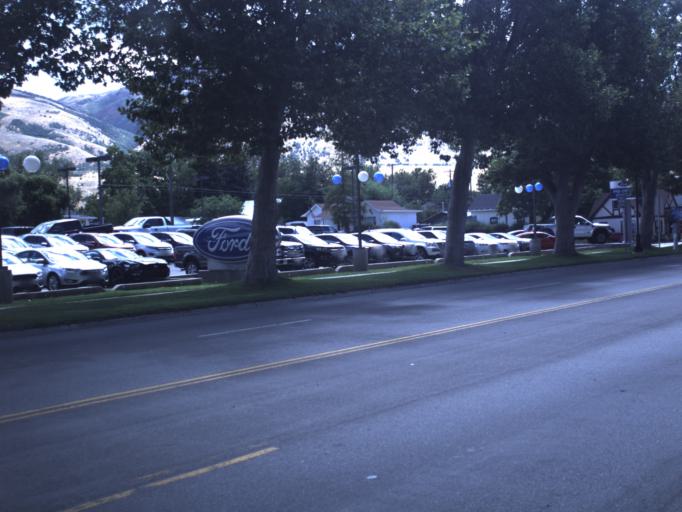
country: US
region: Utah
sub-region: Box Elder County
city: Brigham City
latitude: 41.5038
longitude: -112.0160
